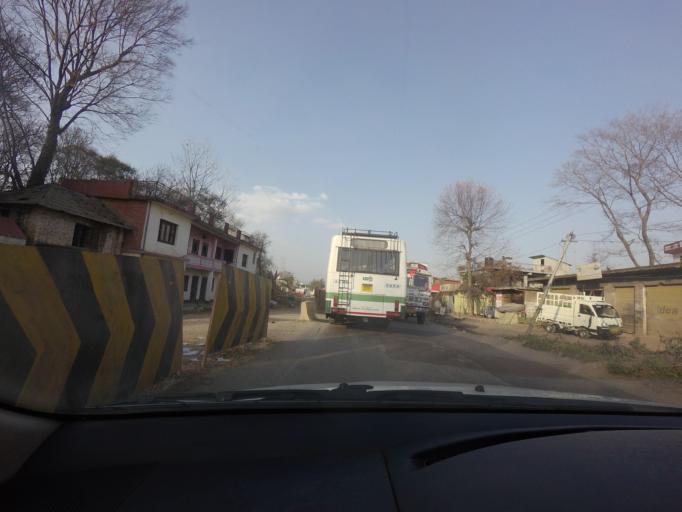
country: IN
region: Himachal Pradesh
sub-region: Mandi
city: Sundarnagar
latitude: 31.5624
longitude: 76.9040
